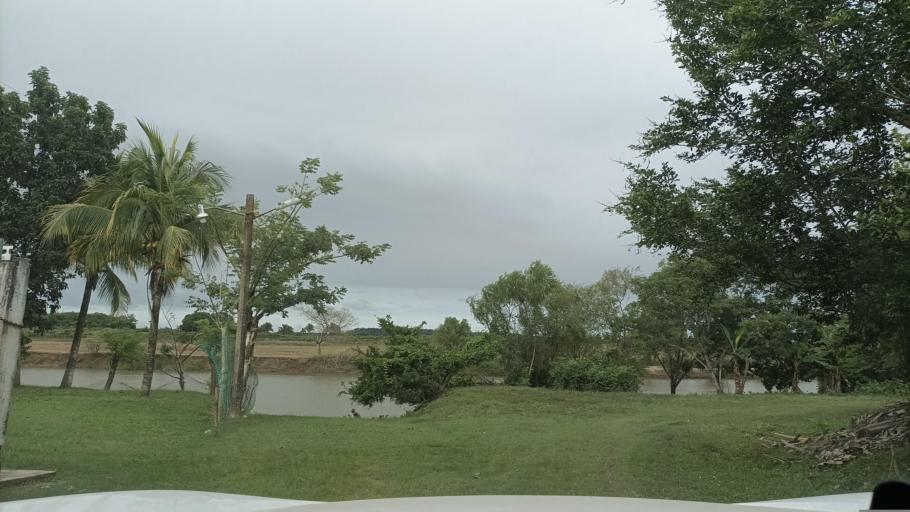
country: MX
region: Veracruz
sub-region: Jaltipan
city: Las Lomas de Tacamichapan
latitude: 17.8628
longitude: -94.7127
